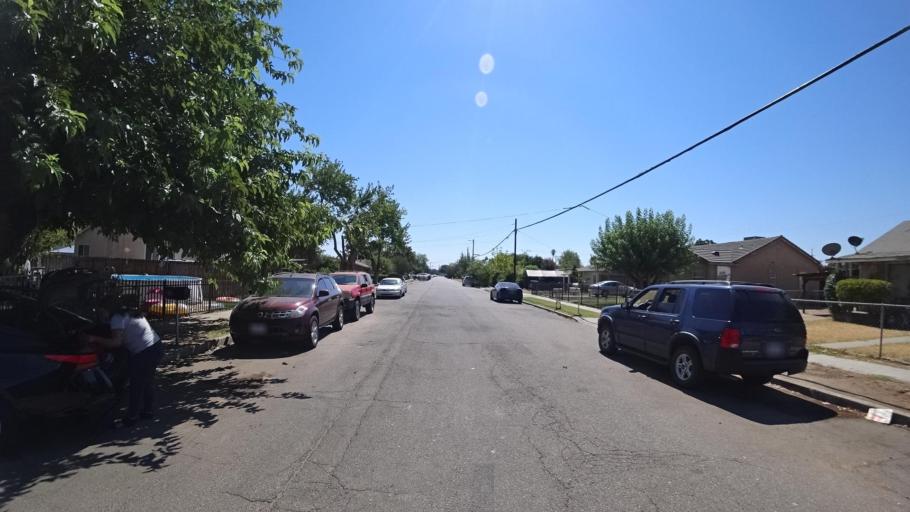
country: US
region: California
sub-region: Fresno County
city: Fresno
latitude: 36.7568
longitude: -119.7403
